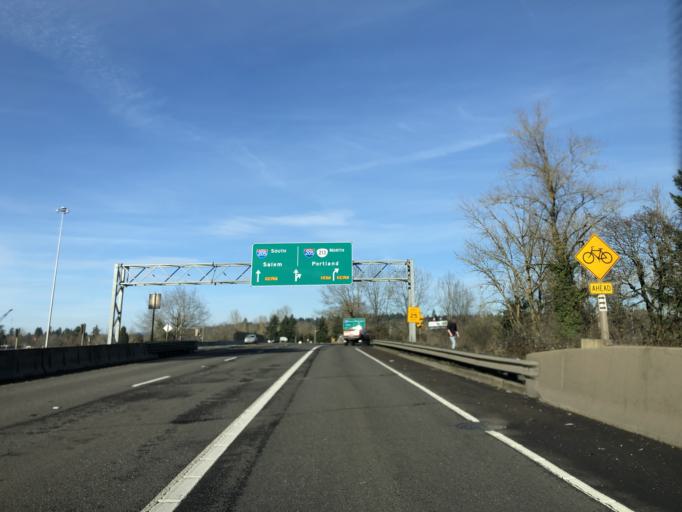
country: US
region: Oregon
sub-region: Clackamas County
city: Gladstone
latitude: 45.3734
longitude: -122.5864
